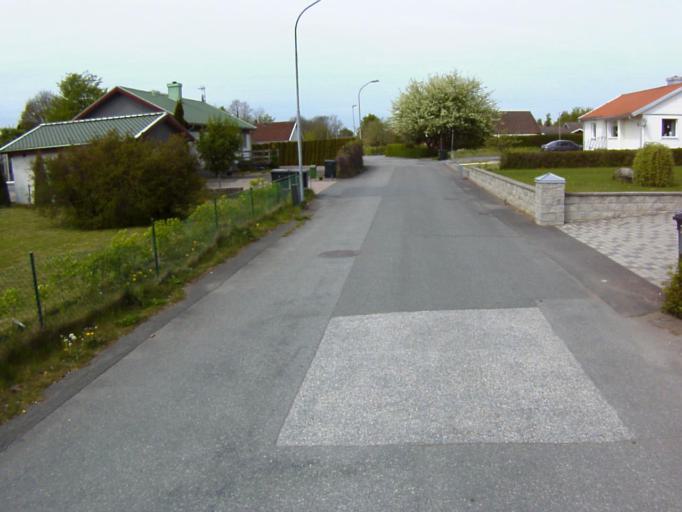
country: SE
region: Skane
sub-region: Kristianstads Kommun
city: Fjalkinge
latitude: 56.0410
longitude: 14.2714
